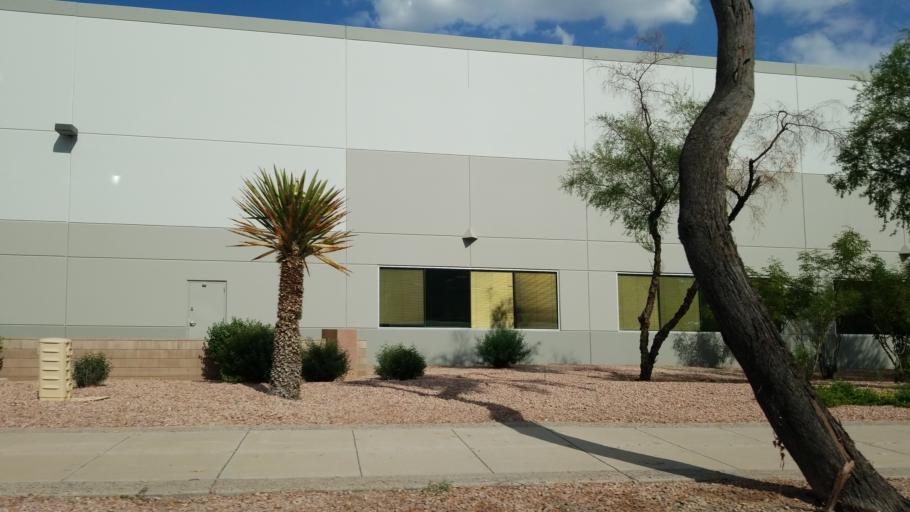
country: US
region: Arizona
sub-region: Maricopa County
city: Guadalupe
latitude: 33.3308
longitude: -111.9455
